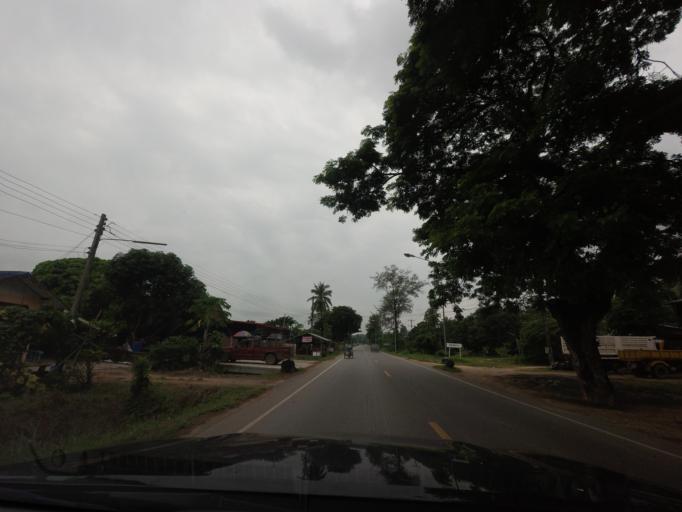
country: TH
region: Nong Khai
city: Si Chiang Mai
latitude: 17.9595
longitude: 102.5473
